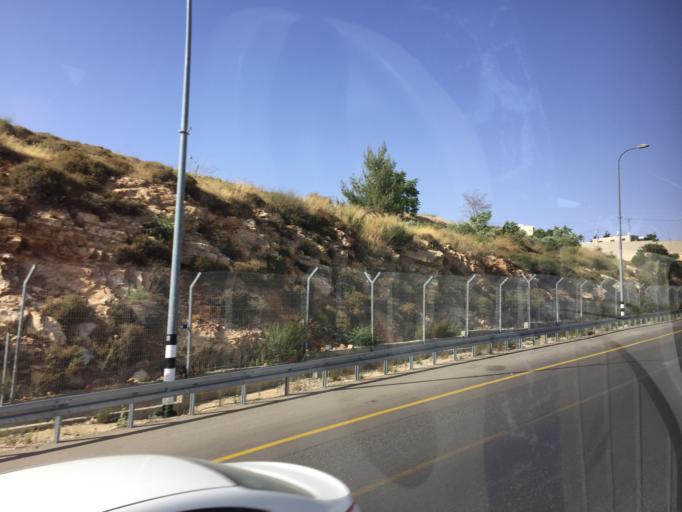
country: PS
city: Khallat Hamamah
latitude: 31.7263
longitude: 35.1936
